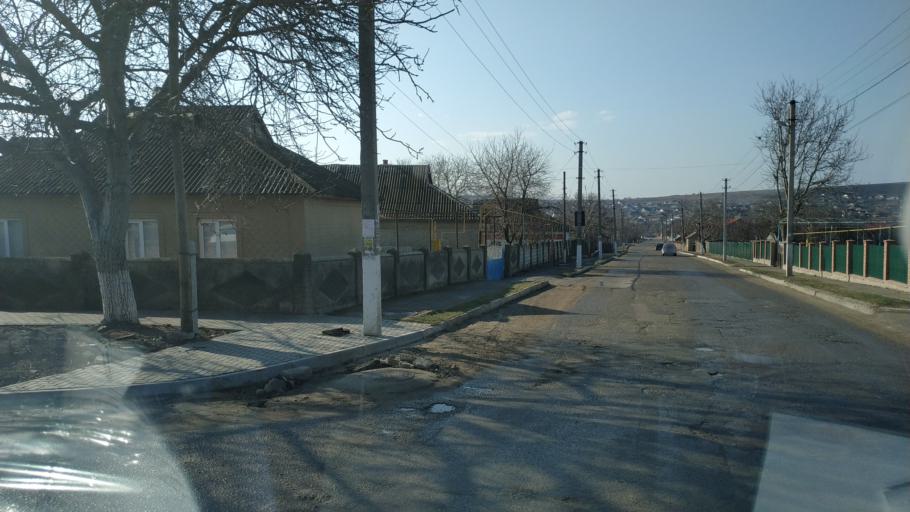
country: MD
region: Chisinau
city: Singera
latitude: 46.6861
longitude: 29.0507
